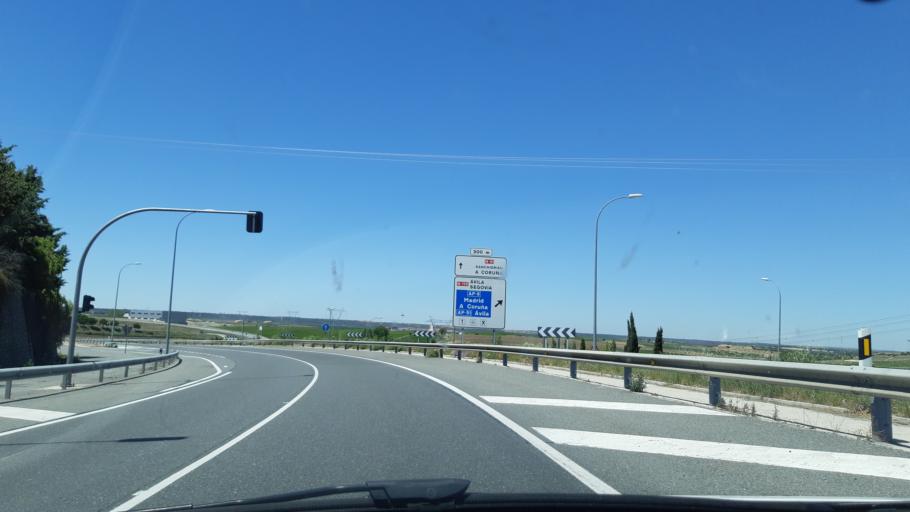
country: ES
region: Castille and Leon
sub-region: Provincia de Segovia
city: Villacastin
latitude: 40.7819
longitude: -4.4113
